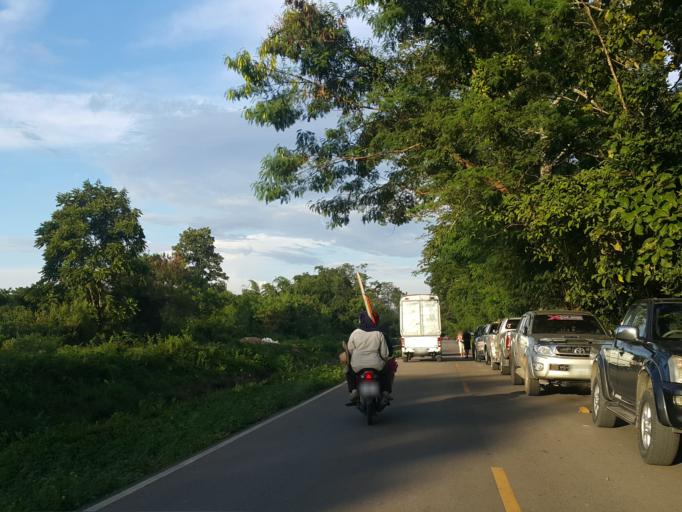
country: TH
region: Chiang Mai
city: San Sai
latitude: 18.8950
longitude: 99.0345
